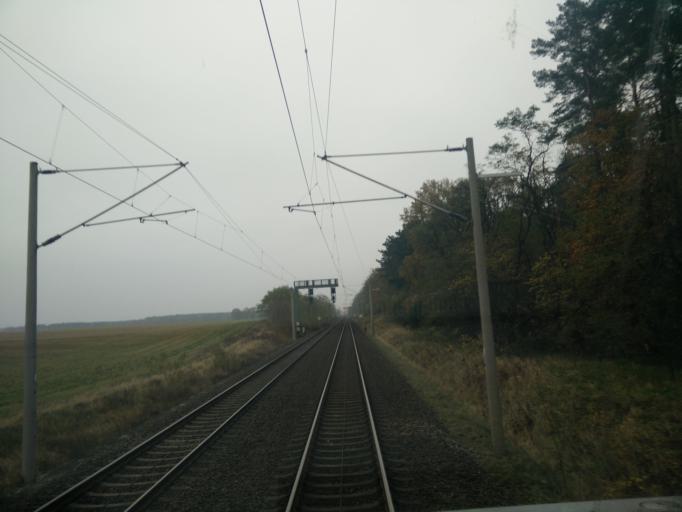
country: DE
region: Brandenburg
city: Retzow
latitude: 52.5910
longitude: 12.6627
